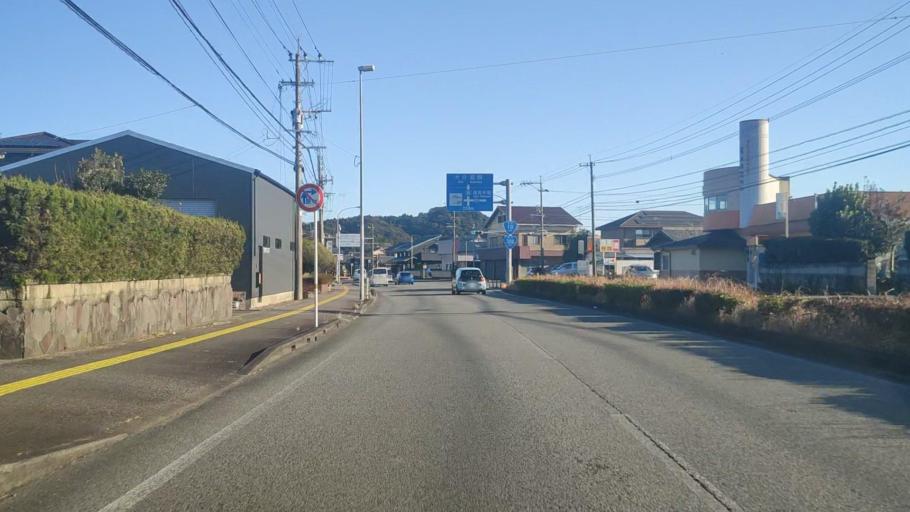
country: JP
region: Miyazaki
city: Nobeoka
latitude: 32.4858
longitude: 131.6629
